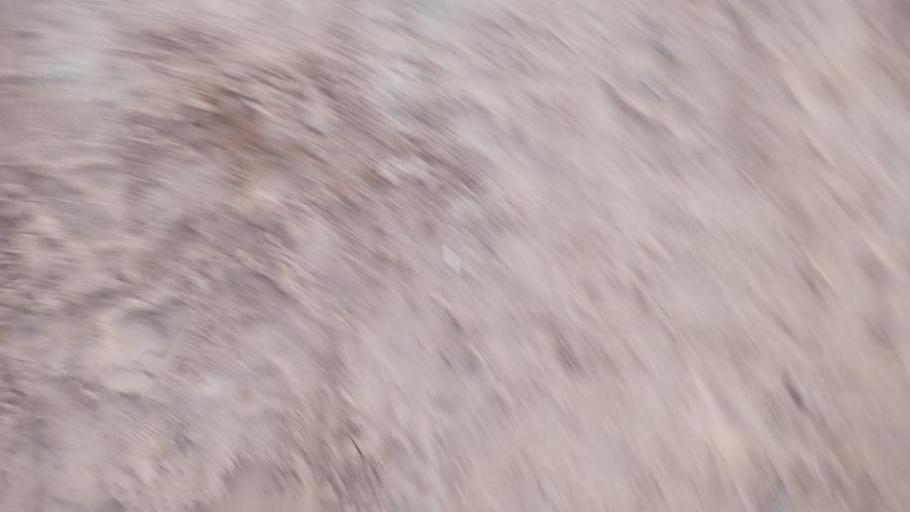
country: TN
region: Madanin
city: Zarzis
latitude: 33.4696
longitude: 11.0840
